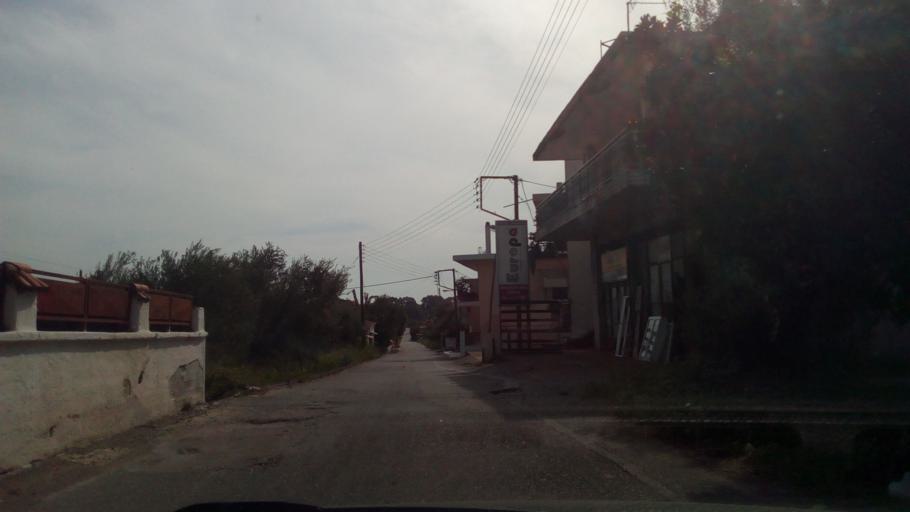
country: GR
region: West Greece
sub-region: Nomos Aitolias kai Akarnanias
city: Nafpaktos
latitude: 38.4024
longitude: 21.8599
